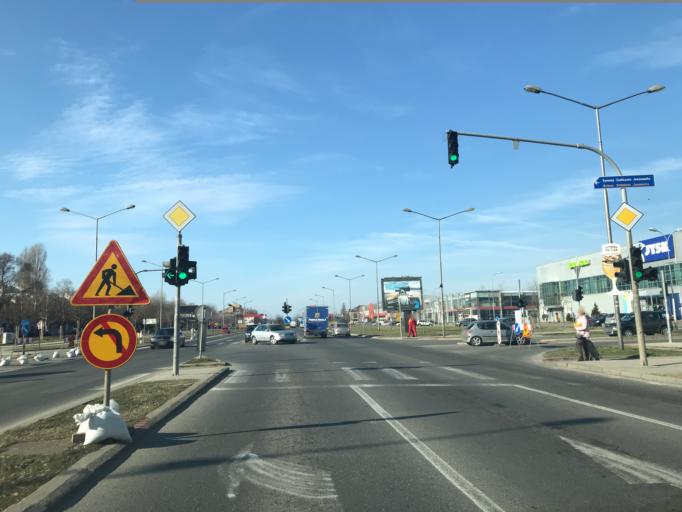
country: RS
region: Autonomna Pokrajina Vojvodina
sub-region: Juznobacki Okrug
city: Novi Sad
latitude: 45.2579
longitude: 19.8017
